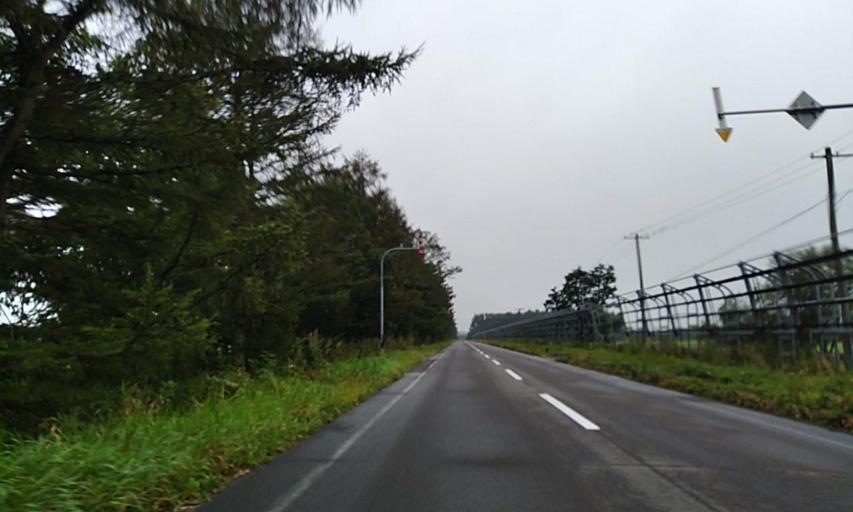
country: JP
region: Hokkaido
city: Shibetsu
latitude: 43.4943
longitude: 144.6456
